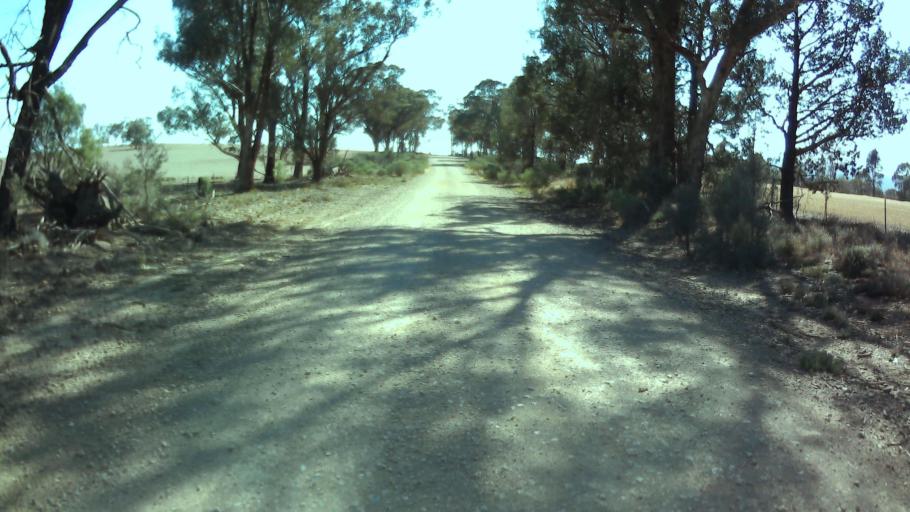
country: AU
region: New South Wales
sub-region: Weddin
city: Grenfell
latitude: -33.9028
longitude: 147.8644
